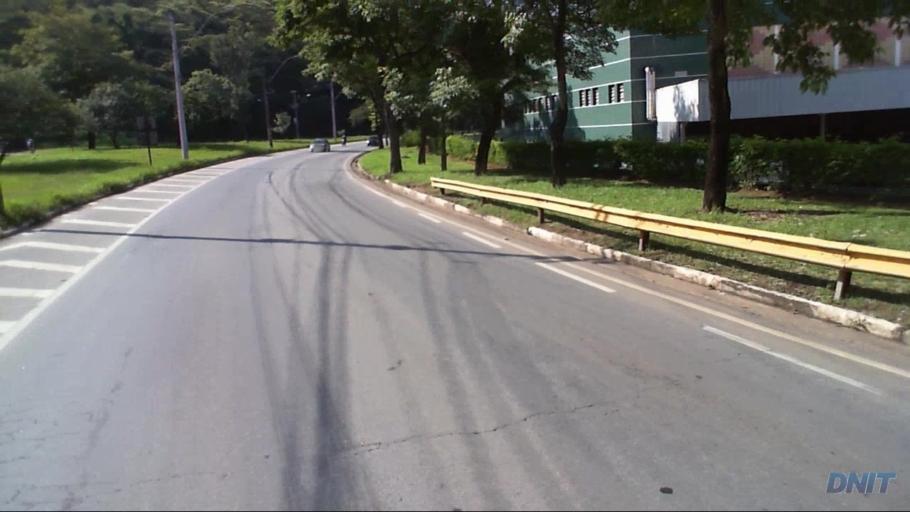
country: BR
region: Minas Gerais
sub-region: Ipatinga
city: Ipatinga
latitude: -19.4973
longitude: -42.5674
